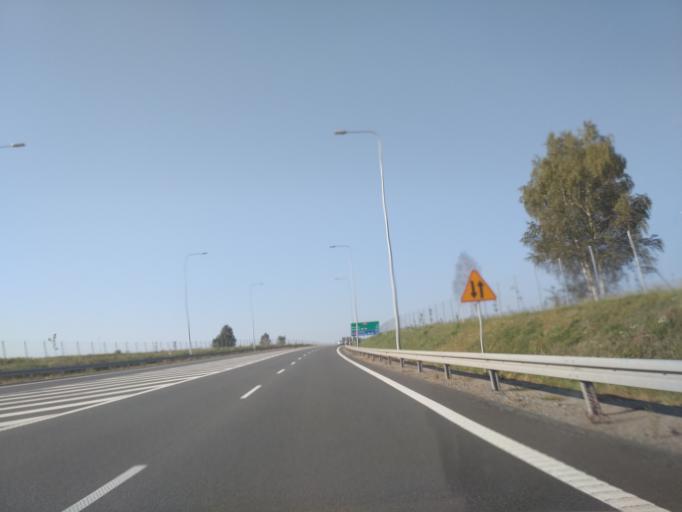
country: PL
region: Subcarpathian Voivodeship
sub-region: Powiat rzeszowski
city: Sokolow Malopolski
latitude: 50.2234
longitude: 22.1368
